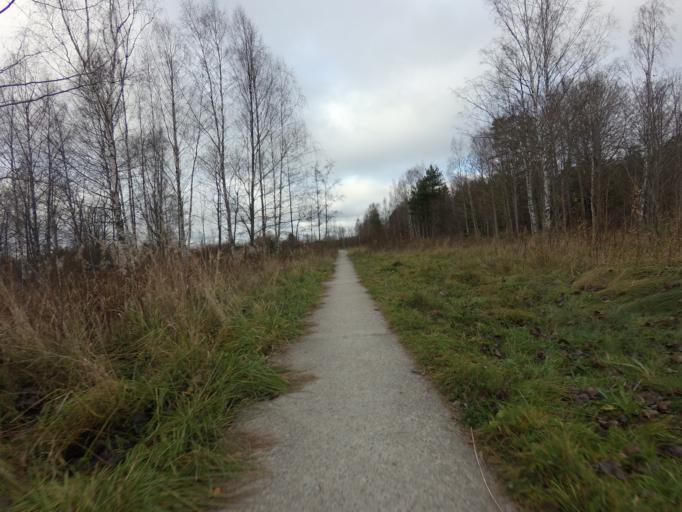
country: FI
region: Uusimaa
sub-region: Helsinki
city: Kauniainen
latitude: 60.1733
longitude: 24.7009
